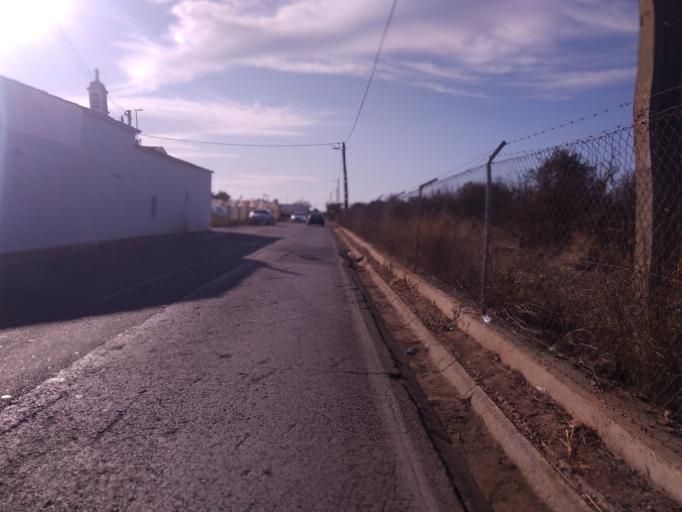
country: PT
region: Faro
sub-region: Faro
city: Faro
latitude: 37.0511
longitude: -7.9280
